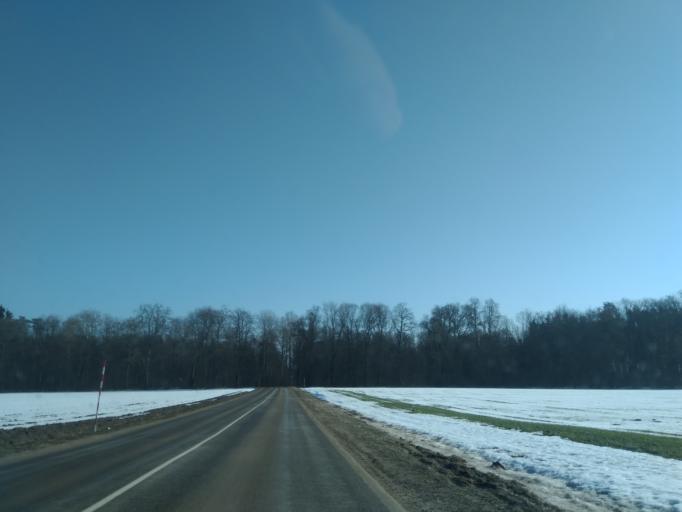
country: BY
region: Minsk
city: Nyasvizh
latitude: 53.2017
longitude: 26.6537
